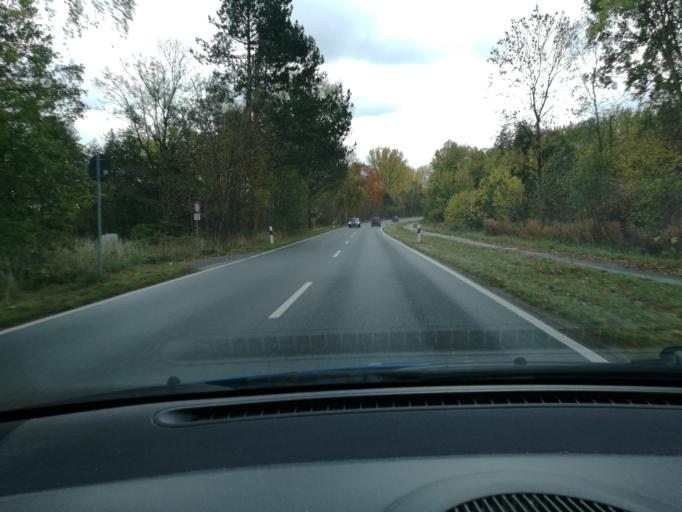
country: DE
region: Schleswig-Holstein
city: Gross Sarau
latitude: 53.7591
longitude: 10.7300
